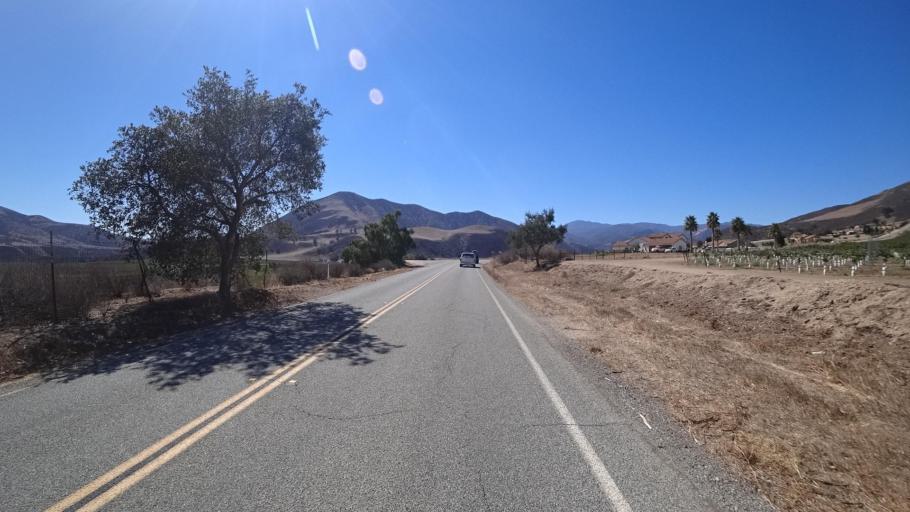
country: US
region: California
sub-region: Monterey County
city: Greenfield
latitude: 36.2873
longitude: -121.3172
